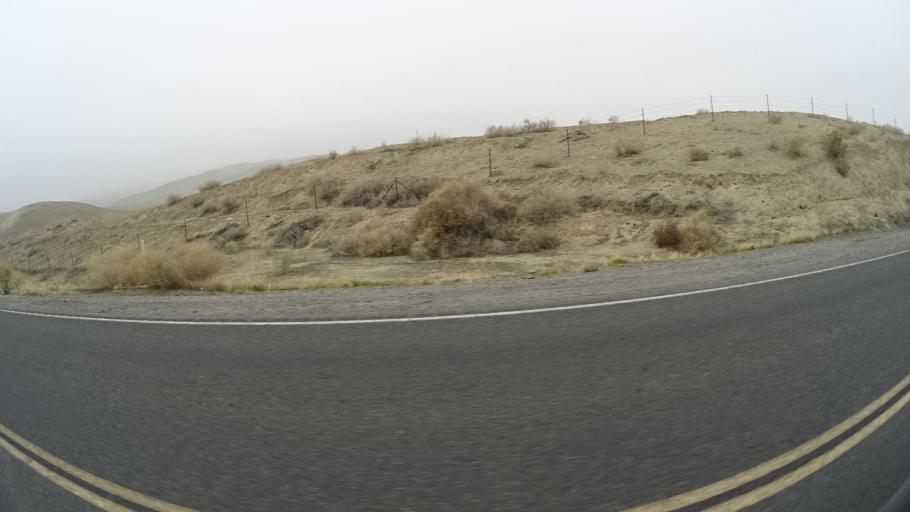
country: US
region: California
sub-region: Kern County
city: Buttonwillow
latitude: 35.3239
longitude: -119.4658
